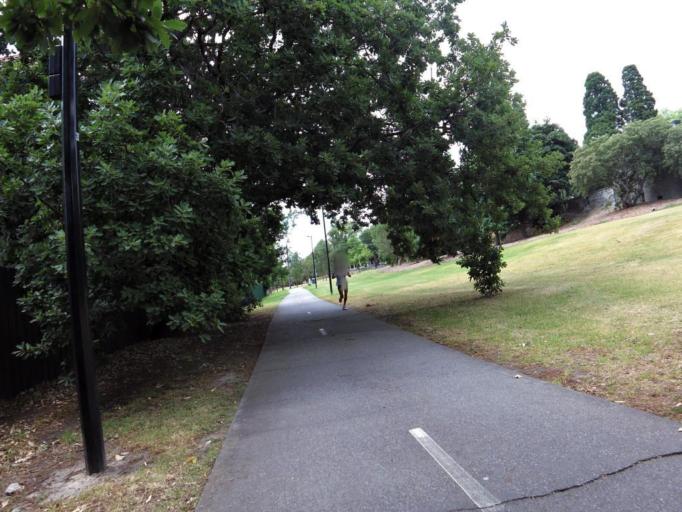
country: AU
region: Victoria
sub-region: Boroondara
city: Kew East
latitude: -37.8035
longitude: 145.0594
